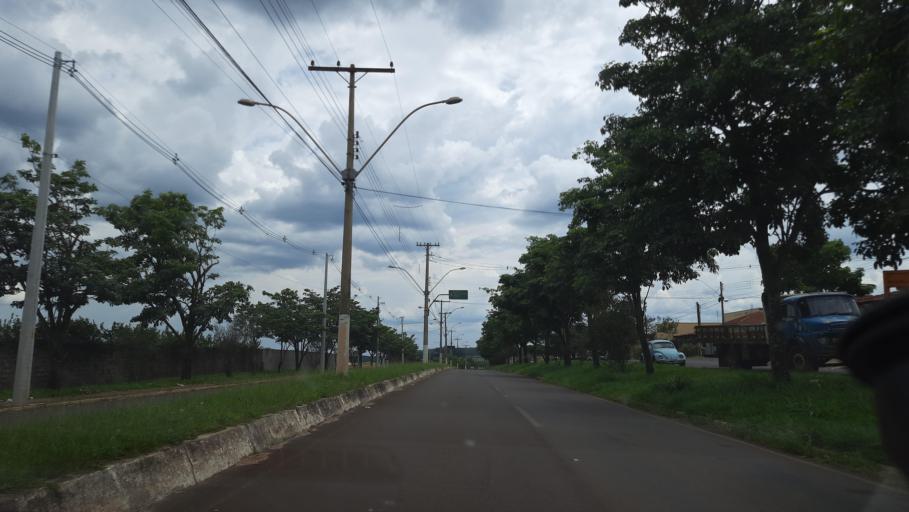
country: BR
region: Sao Paulo
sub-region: Cajuru
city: Cajuru
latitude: -21.2746
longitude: -47.2927
